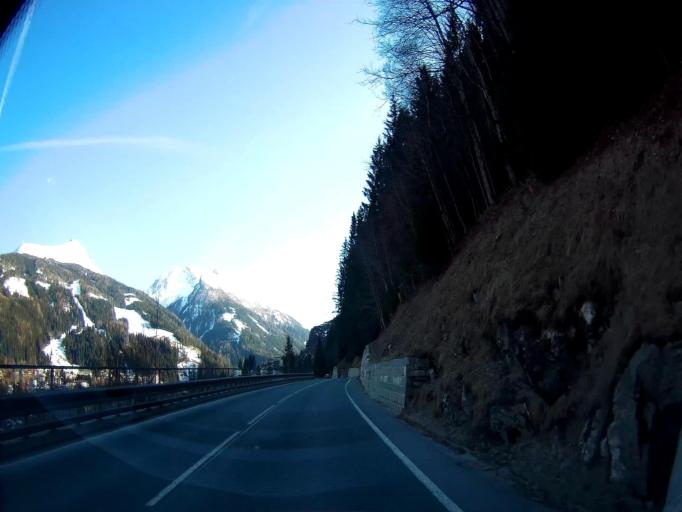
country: AT
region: Salzburg
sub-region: Politischer Bezirk Sankt Johann im Pongau
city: Bad Gastein
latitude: 47.1262
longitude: 13.1310
